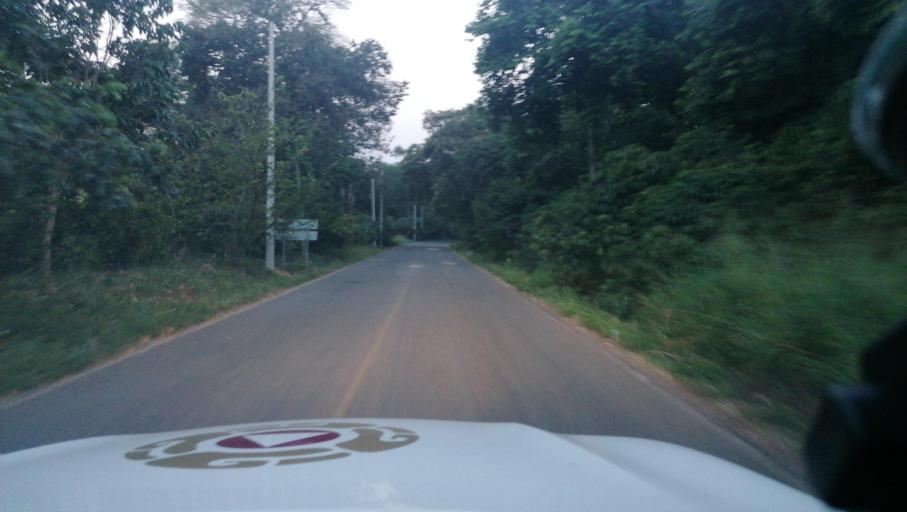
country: MX
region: Chiapas
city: Veinte de Noviembre
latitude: 15.0070
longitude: -92.2459
